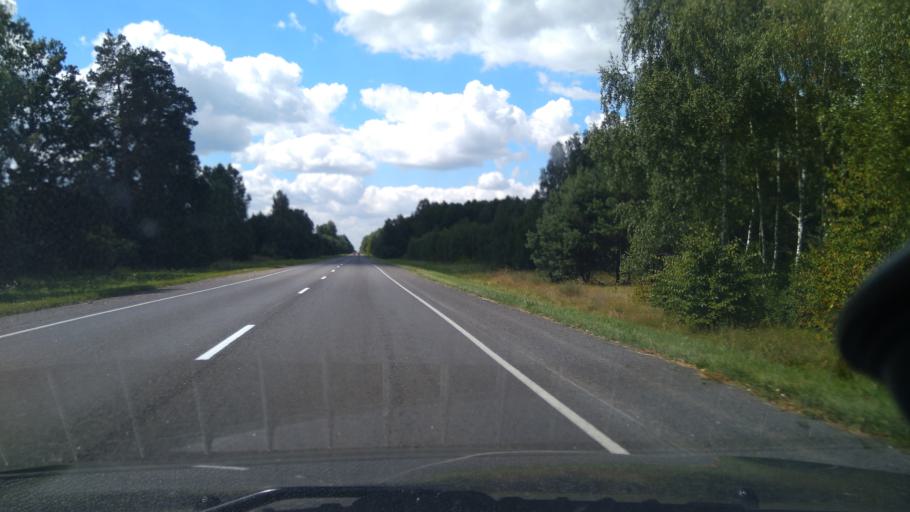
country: BY
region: Brest
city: Nyakhachava
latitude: 52.6700
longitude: 25.2582
